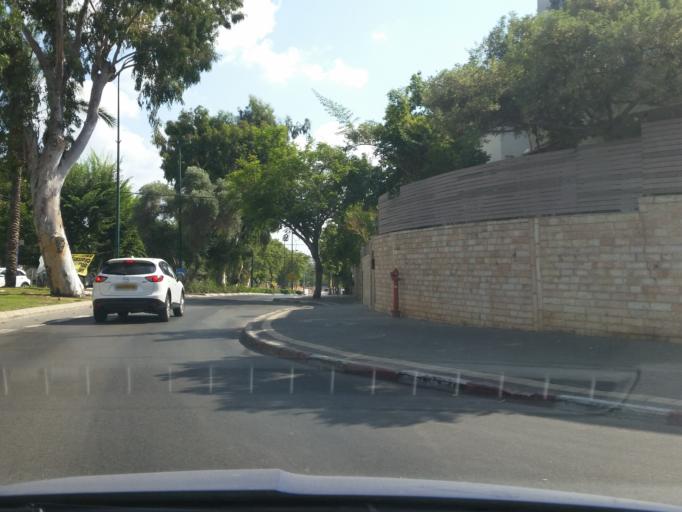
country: IL
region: Tel Aviv
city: Ramat HaSharon
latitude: 32.1148
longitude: 34.8329
